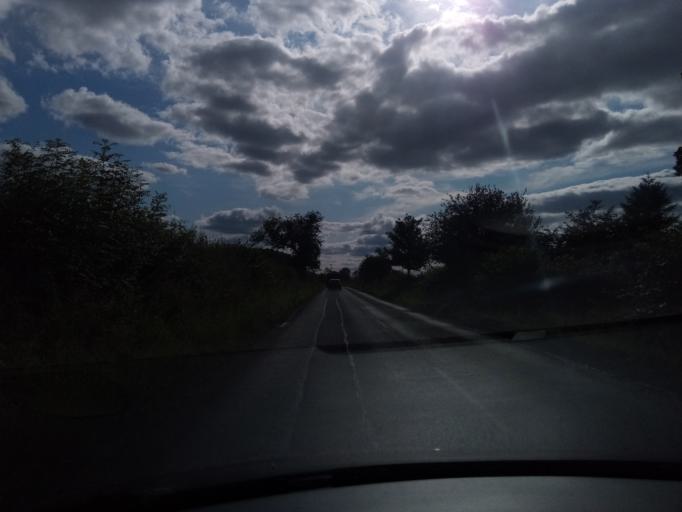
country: GB
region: Scotland
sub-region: The Scottish Borders
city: Coldstream
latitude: 55.7092
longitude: -2.2871
